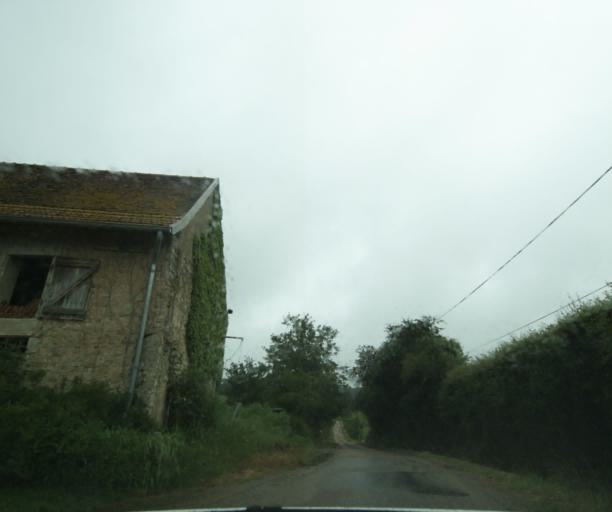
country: FR
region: Bourgogne
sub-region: Departement de Saone-et-Loire
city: Paray-le-Monial
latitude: 46.4711
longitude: 4.1950
